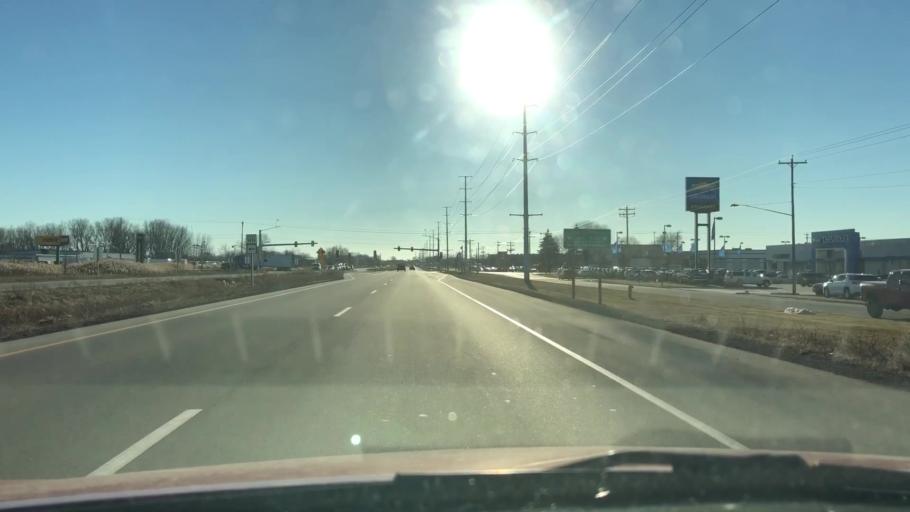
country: US
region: Wisconsin
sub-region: Brown County
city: Ashwaubenon
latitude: 44.4740
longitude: -88.0631
